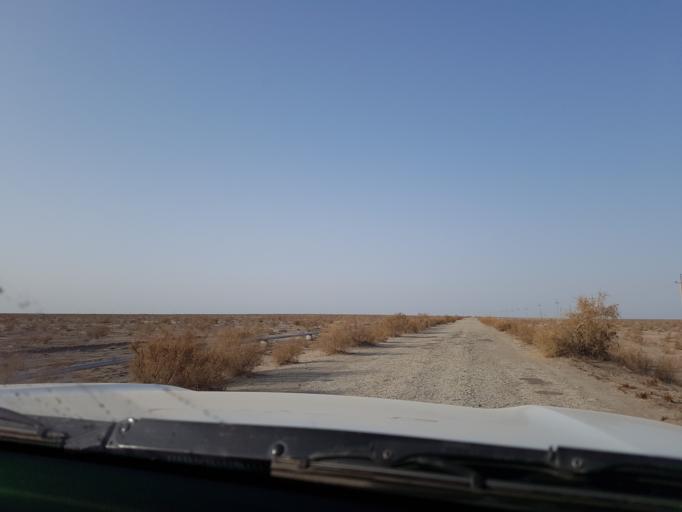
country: UZ
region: Karakalpakstan
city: Shumanay Shahri
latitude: 42.0078
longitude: 58.0855
